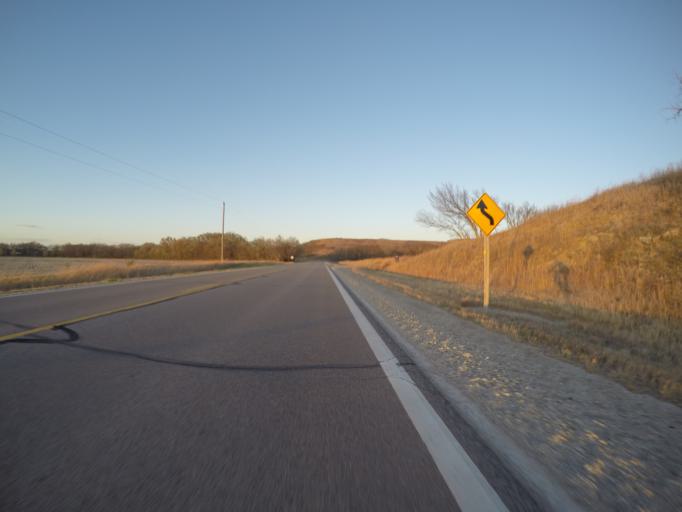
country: US
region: Kansas
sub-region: Riley County
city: Manhattan
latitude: 39.1244
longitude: -96.5689
